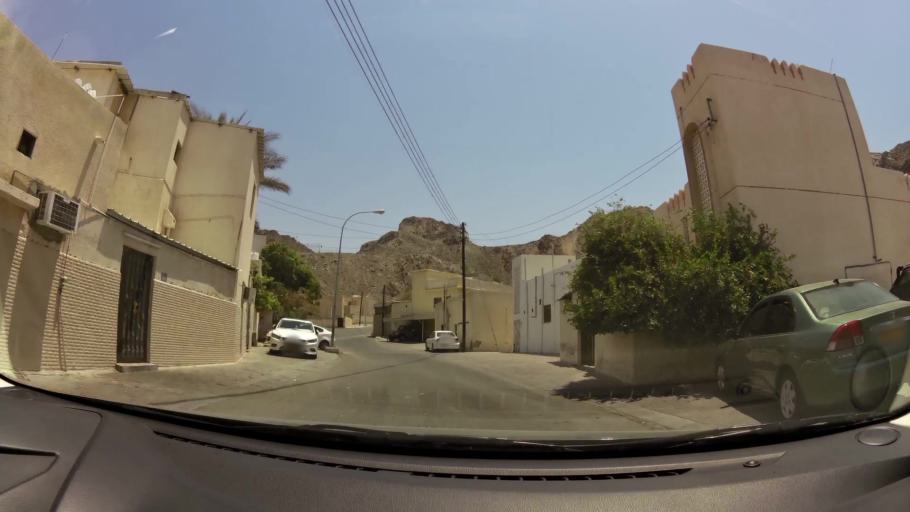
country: OM
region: Muhafazat Masqat
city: Muscat
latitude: 23.6185
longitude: 58.5530
